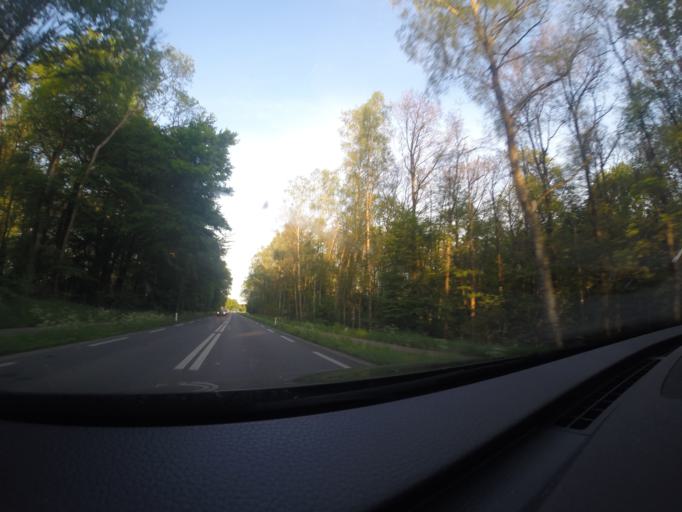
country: NL
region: Gelderland
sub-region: Gemeente Voorst
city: Voorst
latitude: 52.1840
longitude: 6.1219
